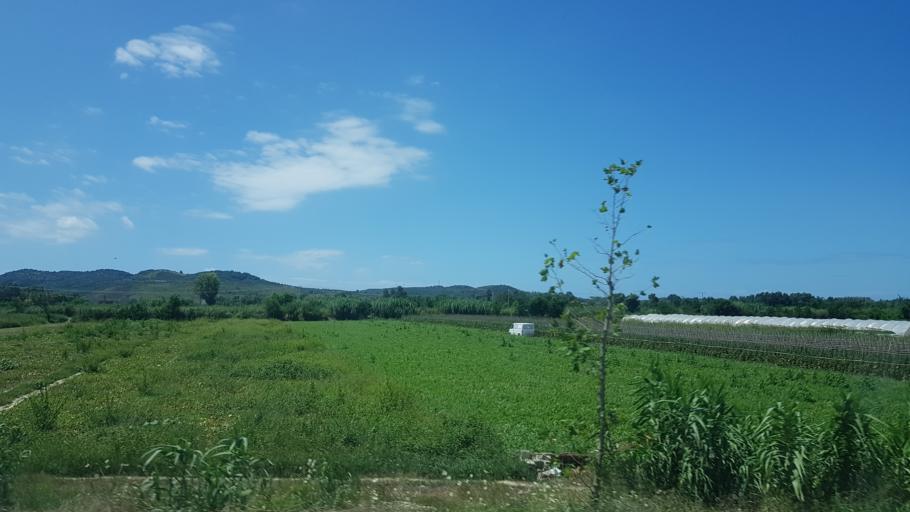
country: AL
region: Fier
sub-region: Rrethi i Fierit
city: Frakulla e Madhe
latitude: 40.6136
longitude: 19.5228
